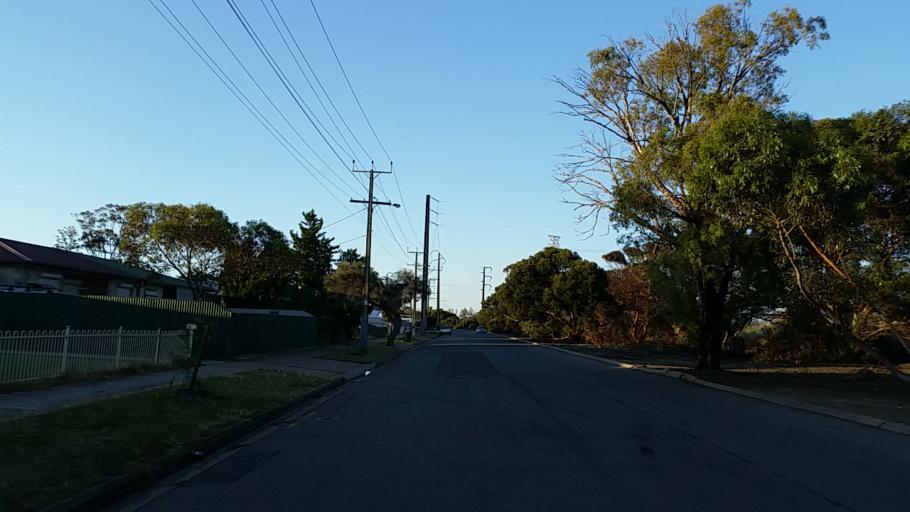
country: AU
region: South Australia
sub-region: Port Adelaide Enfield
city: Birkenhead
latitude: -34.8072
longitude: 138.5065
